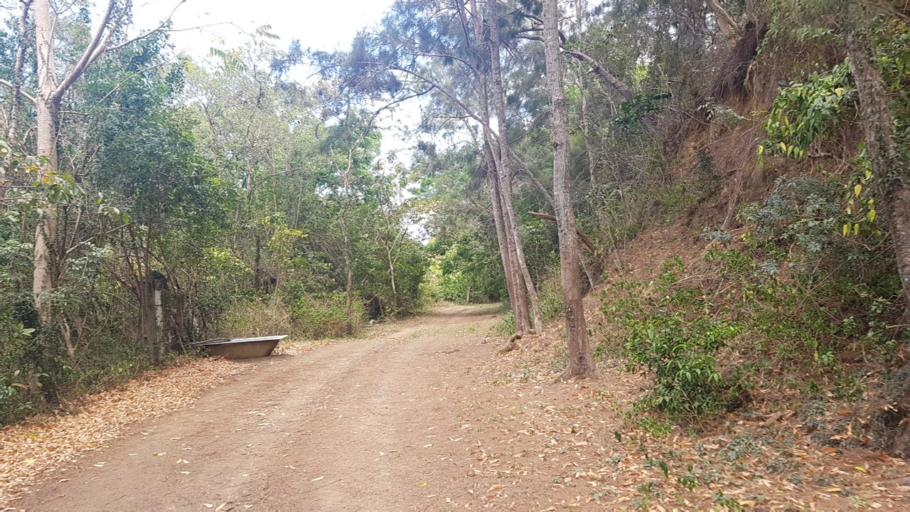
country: NC
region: South Province
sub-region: Dumbea
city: Dumbea
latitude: -22.1779
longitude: 166.4778
